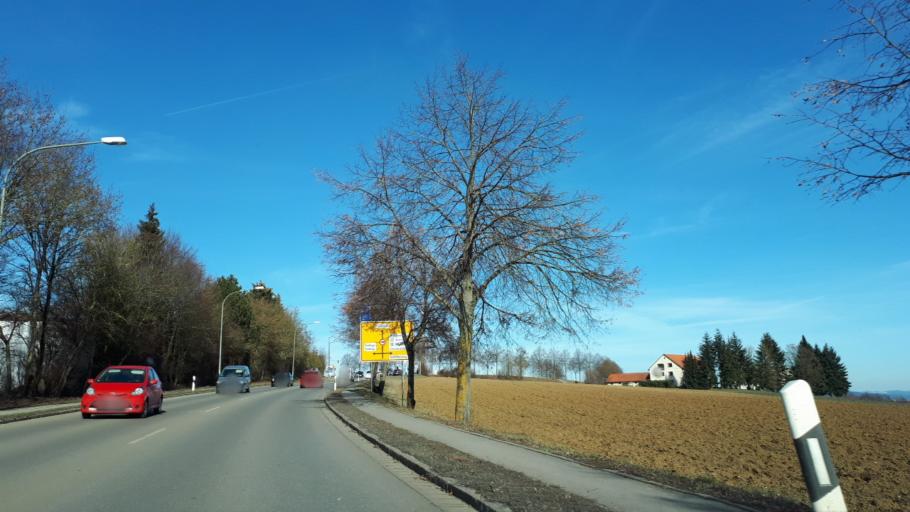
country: DE
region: Bavaria
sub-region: Upper Palatinate
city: Pentling
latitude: 48.9871
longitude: 12.0663
